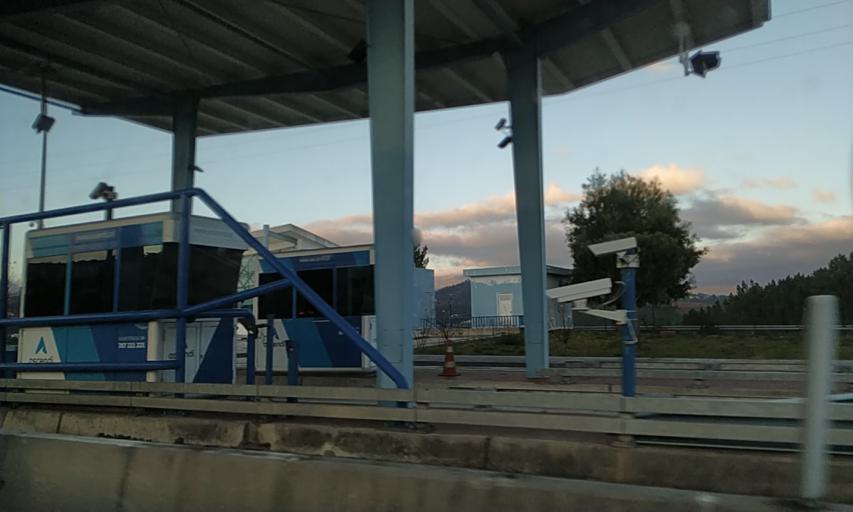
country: PT
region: Braga
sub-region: Cabeceiras de Basto
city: Cabeceiras de Basto
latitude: 41.4760
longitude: -7.9487
